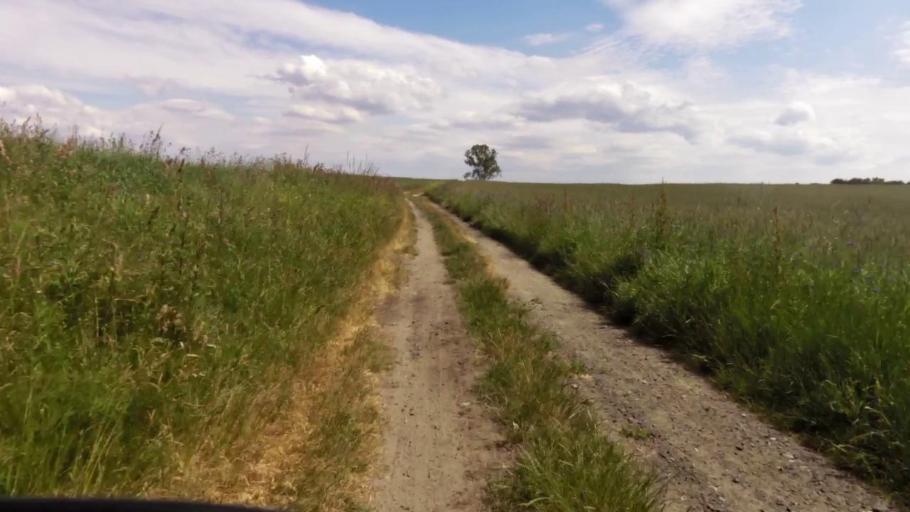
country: PL
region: West Pomeranian Voivodeship
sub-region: Powiat kamienski
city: Wolin
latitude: 53.8577
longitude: 14.5603
